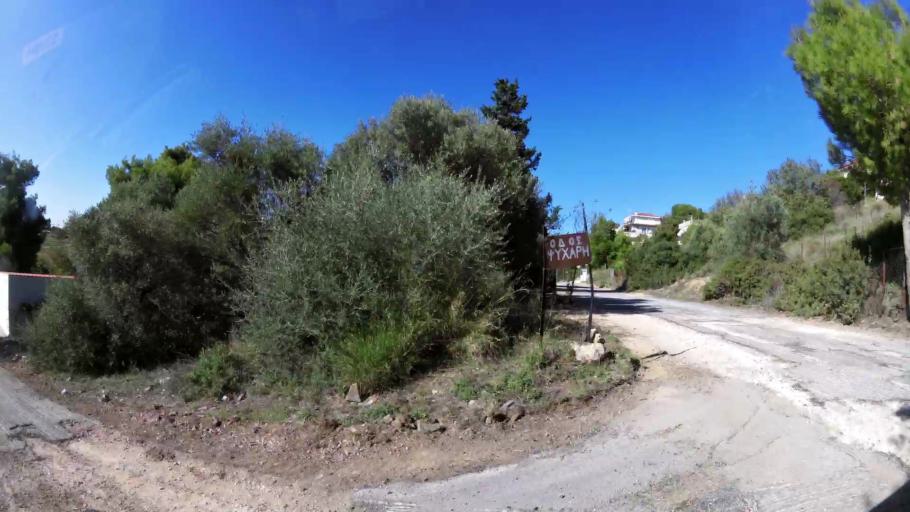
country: GR
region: Attica
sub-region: Nomarchia Anatolikis Attikis
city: Anthousa
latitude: 38.0171
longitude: 23.8780
